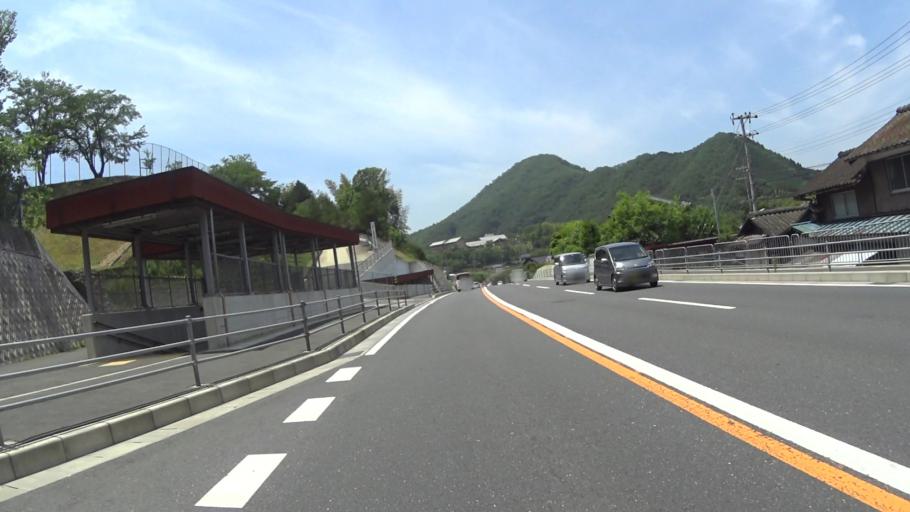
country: JP
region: Kyoto
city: Ayabe
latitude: 35.2204
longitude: 135.2276
